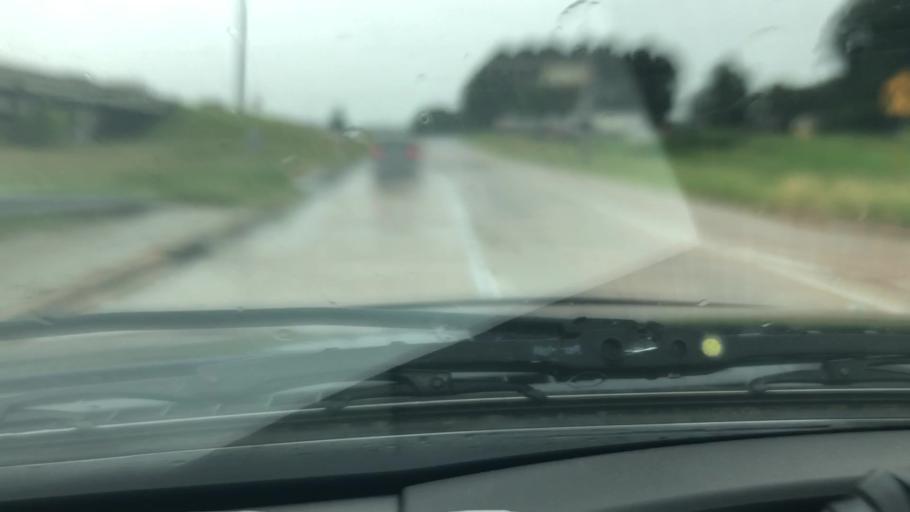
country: US
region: Texas
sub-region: Bowie County
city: Wake Village
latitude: 33.4311
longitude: -94.0973
